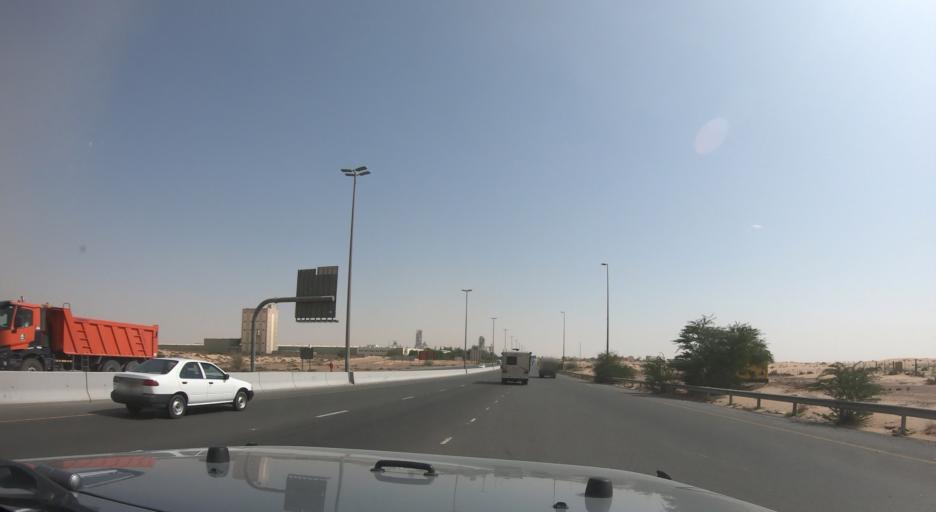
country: AE
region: Ash Shariqah
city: Sharjah
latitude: 25.2999
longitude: 55.6002
